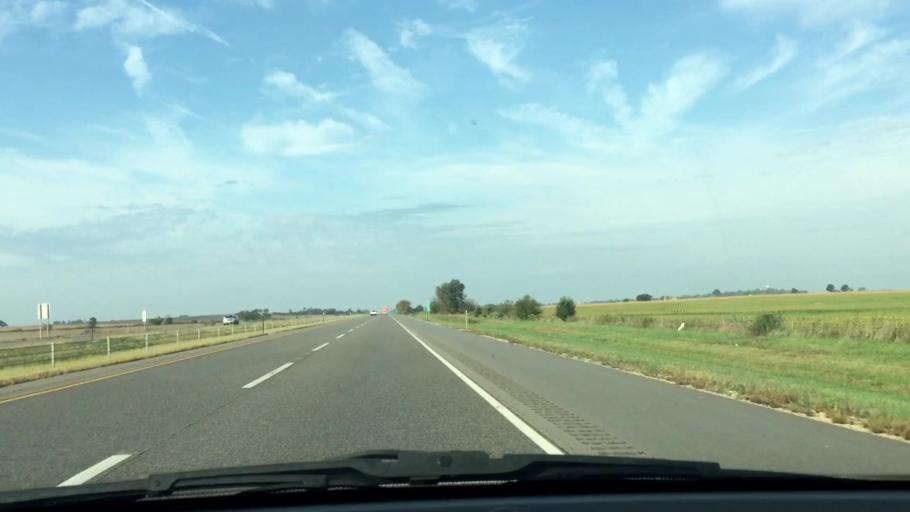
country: US
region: Illinois
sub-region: Ogle County
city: Rochelle
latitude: 41.8688
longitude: -89.1717
